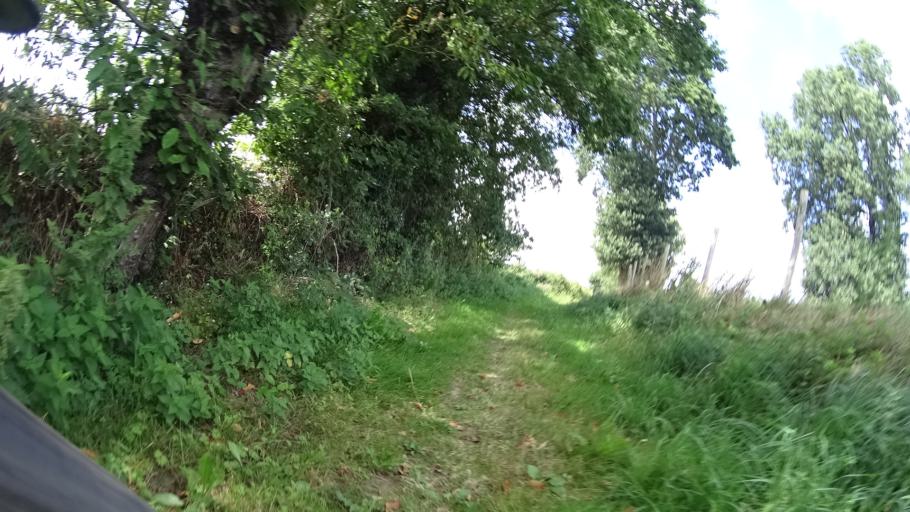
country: FR
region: Brittany
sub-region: Departement d'Ille-et-Vilaine
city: La Meziere
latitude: 48.2197
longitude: -1.7382
